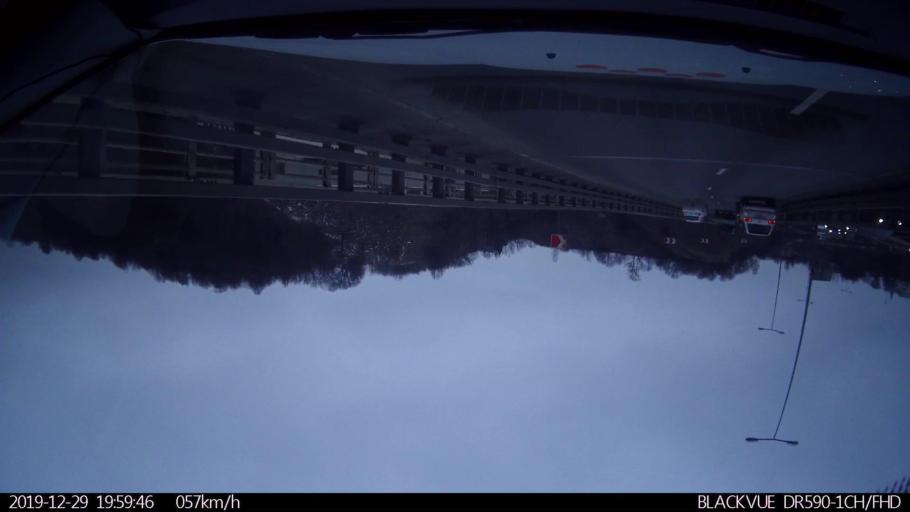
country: RU
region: Nizjnij Novgorod
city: Nizhniy Novgorod
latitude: 56.3203
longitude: 43.9678
